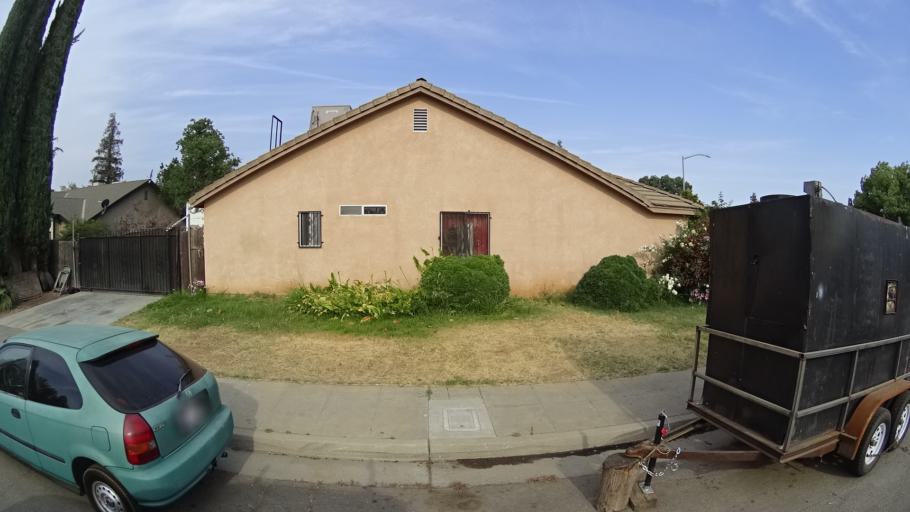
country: US
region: California
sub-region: Fresno County
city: West Park
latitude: 36.7735
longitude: -119.8681
